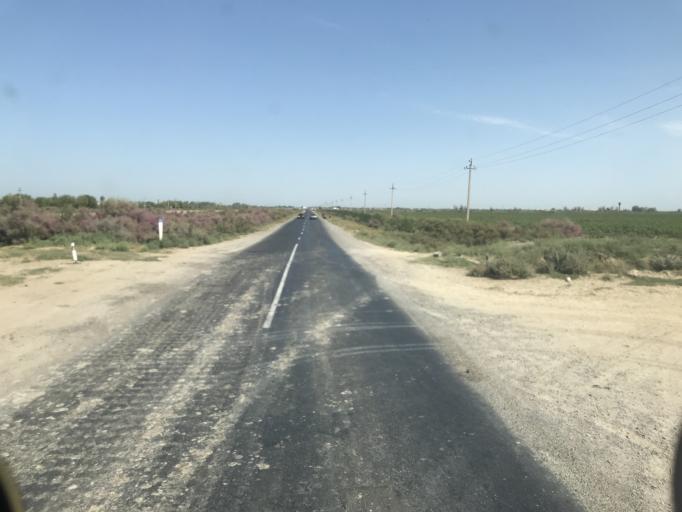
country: KZ
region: Ongtustik Qazaqstan
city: Myrzakent
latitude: 40.7335
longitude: 68.5366
